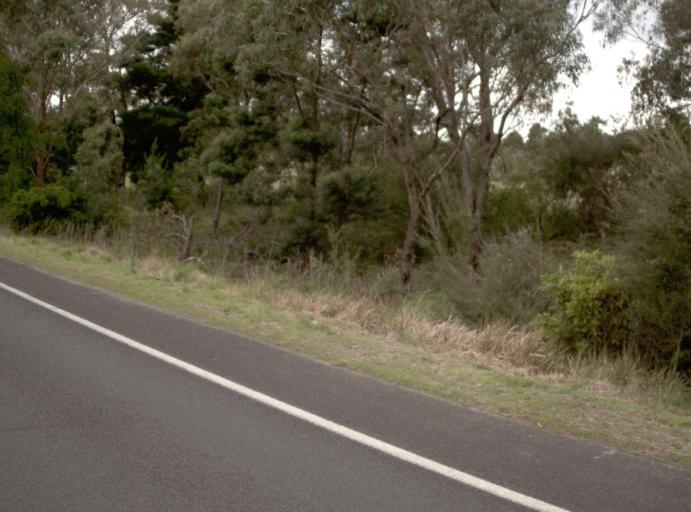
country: AU
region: Victoria
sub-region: Wellington
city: Sale
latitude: -38.1825
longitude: 147.0827
